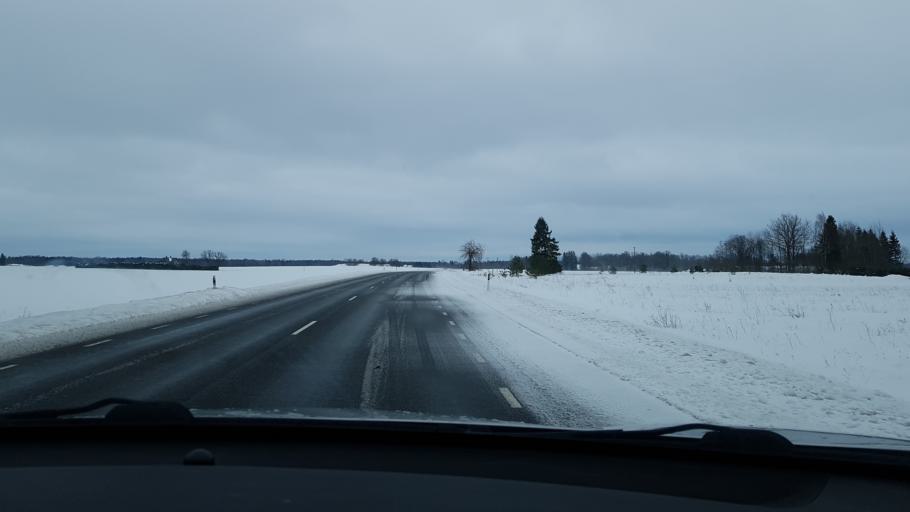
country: EE
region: Jaervamaa
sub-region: Jaerva-Jaani vald
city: Jarva-Jaani
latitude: 59.0905
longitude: 25.8316
